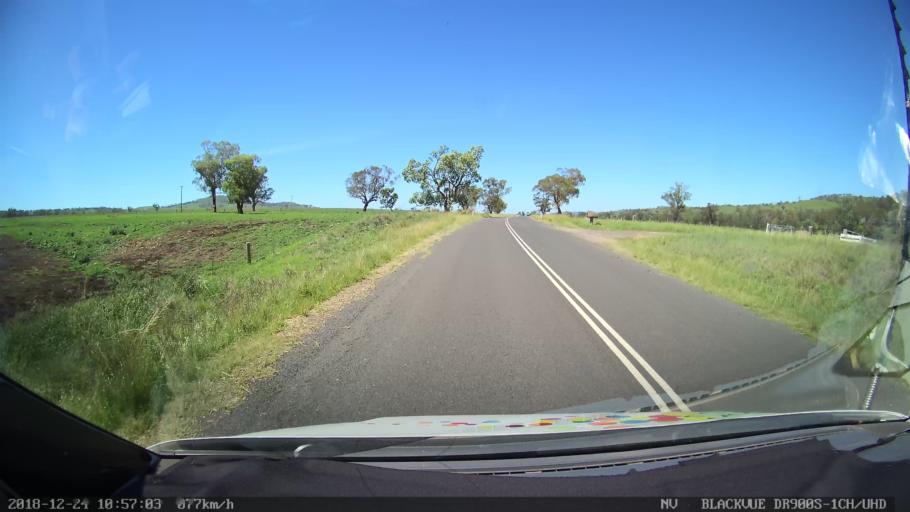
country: AU
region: New South Wales
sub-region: Upper Hunter Shire
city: Merriwa
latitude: -32.0321
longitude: 150.4160
